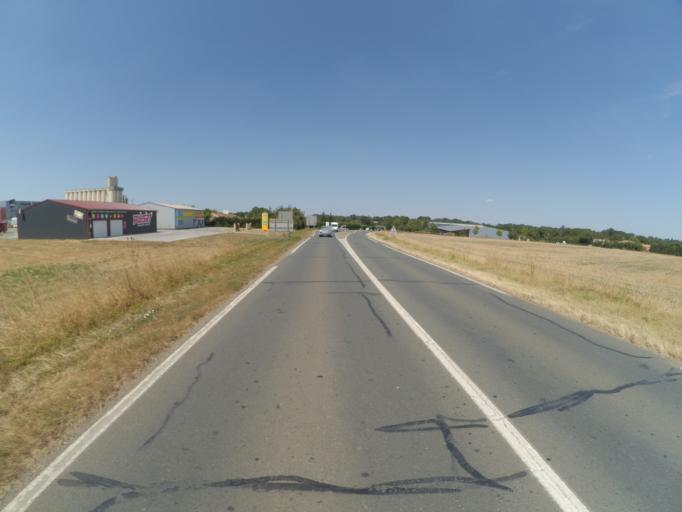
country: FR
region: Poitou-Charentes
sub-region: Departement de la Vienne
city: Lusignan
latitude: 46.4284
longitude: 0.1101
